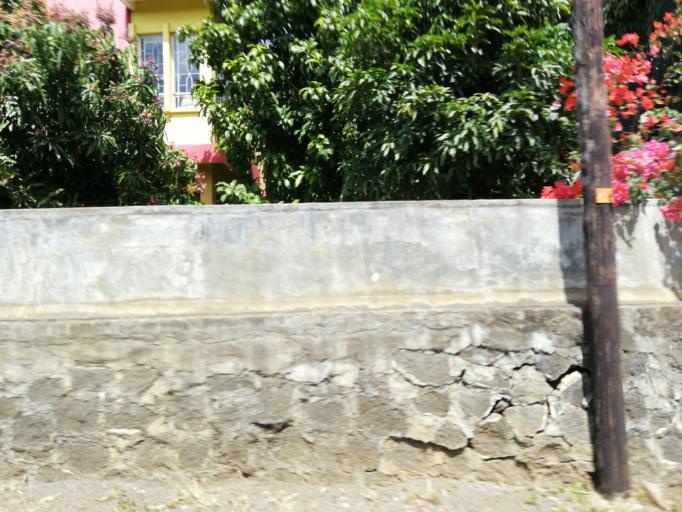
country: MU
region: Plaines Wilhems
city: Ebene
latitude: -20.2356
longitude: 57.4667
